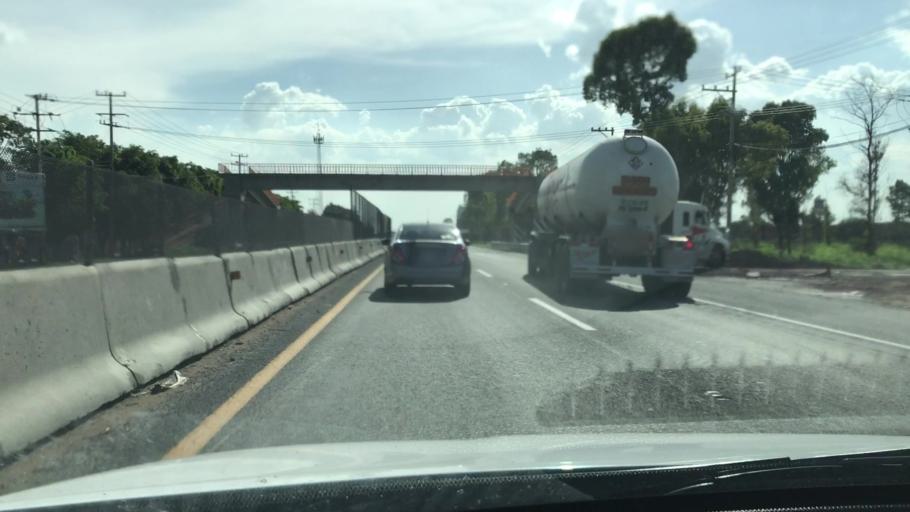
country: MX
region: Guanajuato
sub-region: Cortazar
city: Colonia la Calzada (La Olla)
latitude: 20.5102
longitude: -100.9679
